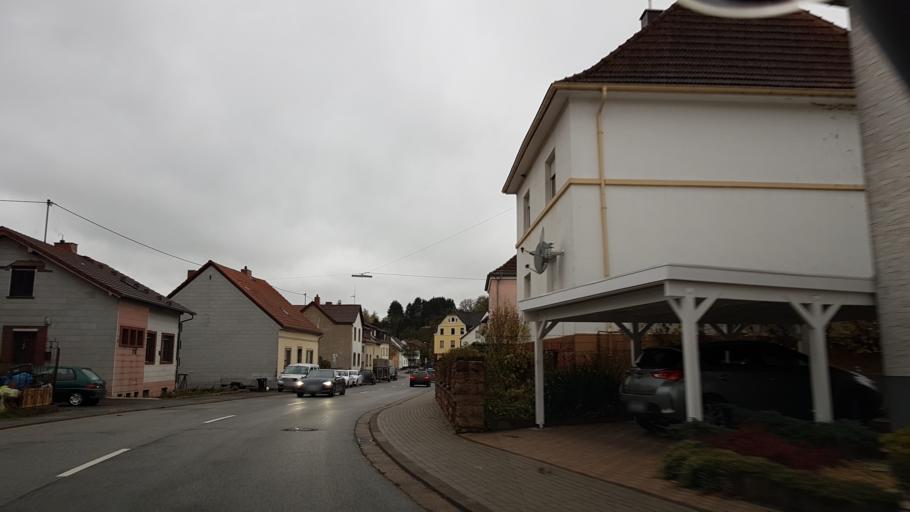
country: DE
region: Saarland
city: Hangard
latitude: 49.3839
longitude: 7.2119
